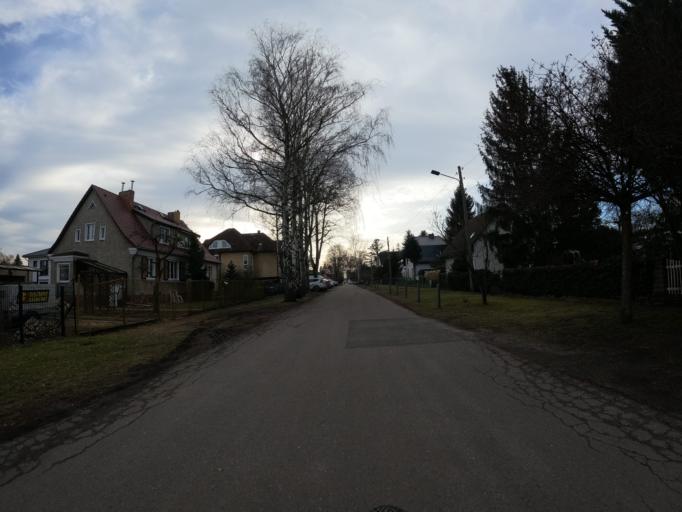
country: DE
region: Brandenburg
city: Hoppegarten
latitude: 52.5244
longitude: 13.6393
